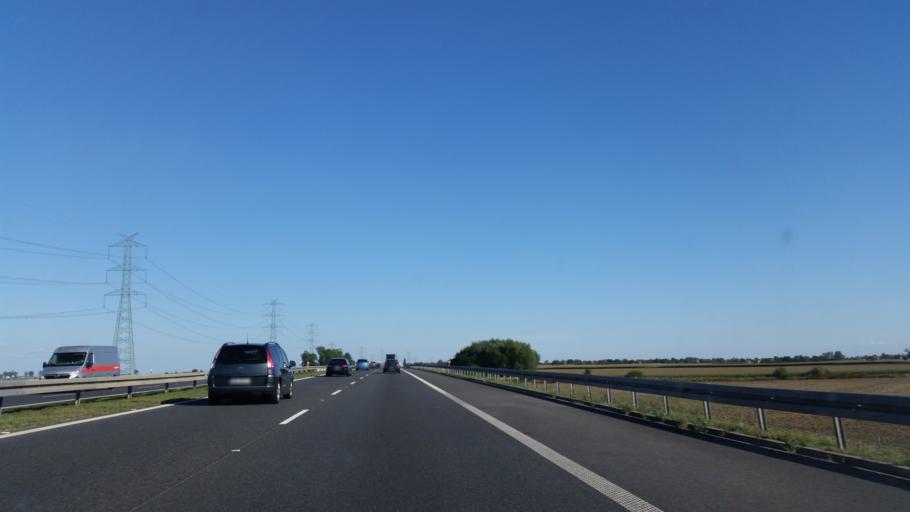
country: PL
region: Lower Silesian Voivodeship
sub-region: Powiat olawski
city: Wierzbno
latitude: 50.9051
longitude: 17.1624
